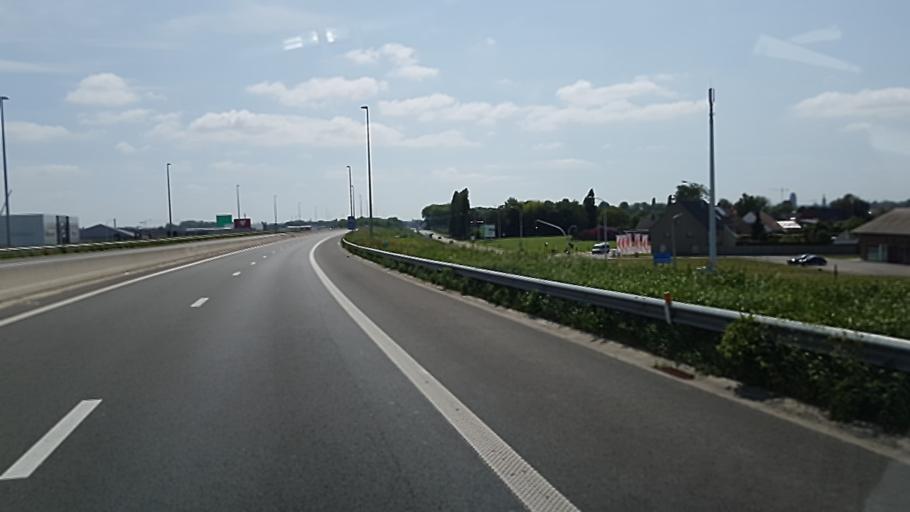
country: BE
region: Flanders
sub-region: Provincie West-Vlaanderen
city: Kortrijk
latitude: 50.8528
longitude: 3.2504
